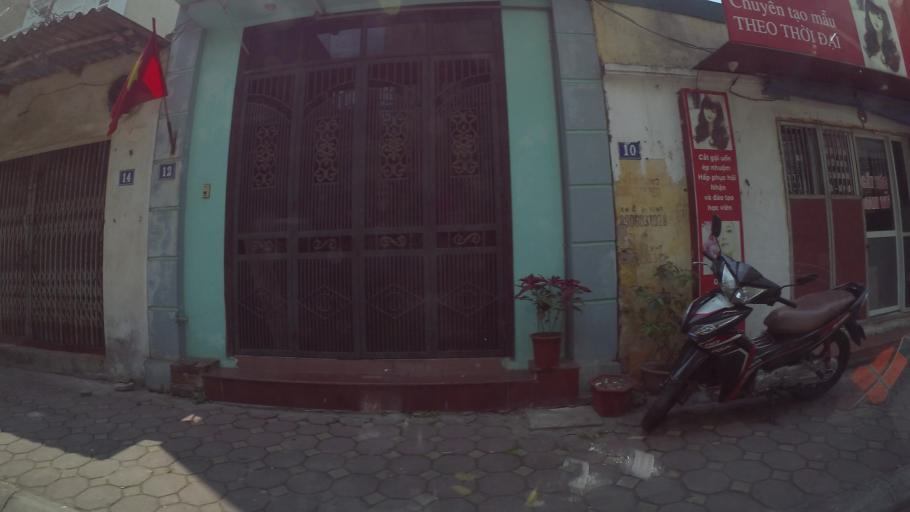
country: VN
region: Ha Noi
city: Trau Quy
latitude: 21.0302
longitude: 105.9082
